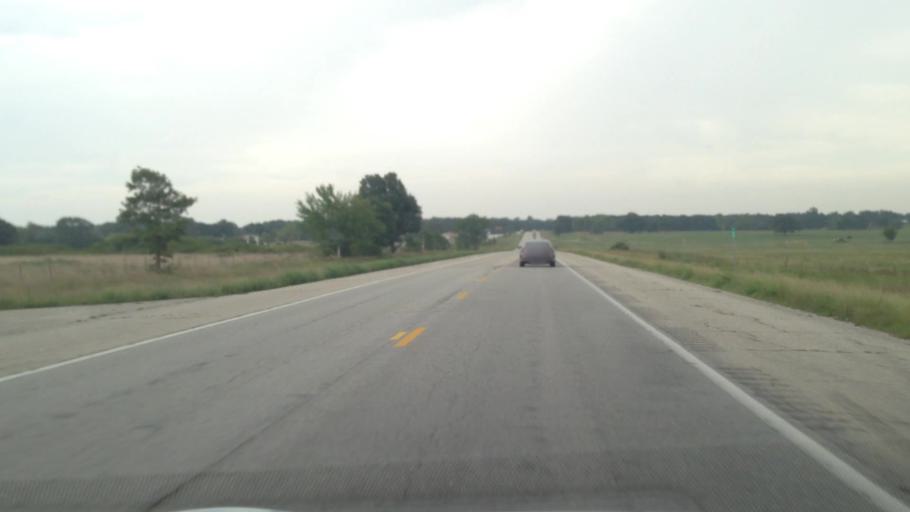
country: US
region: Kansas
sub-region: Cherokee County
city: Galena
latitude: 37.0128
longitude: -94.6291
